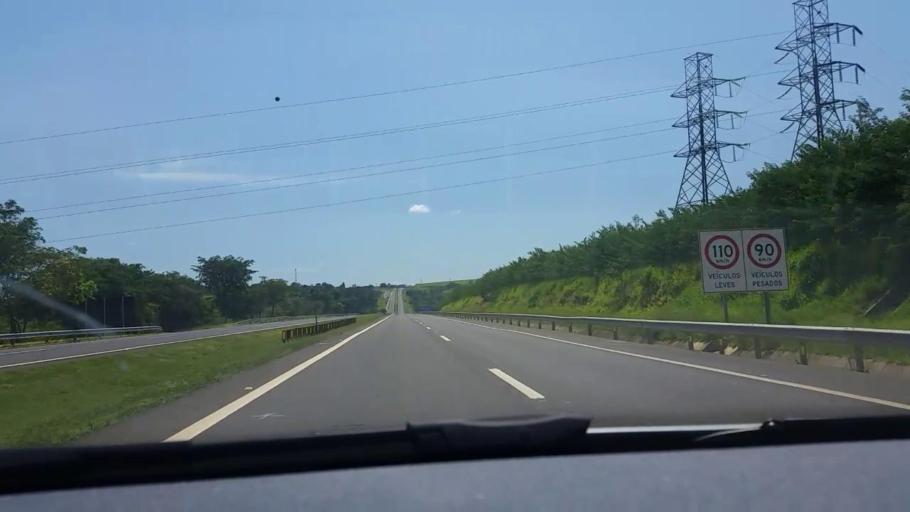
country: BR
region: Sao Paulo
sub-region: Bauru
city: Bauru
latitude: -22.4119
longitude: -49.1034
